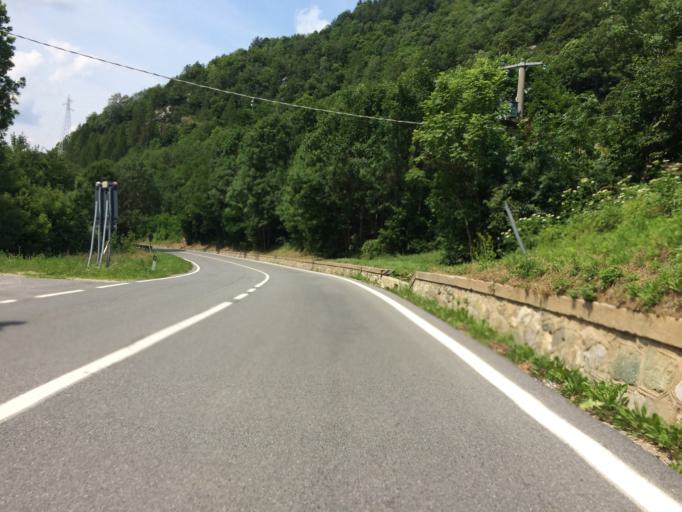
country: IT
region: Piedmont
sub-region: Provincia di Cuneo
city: Vernante
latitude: 44.2304
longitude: 7.5558
